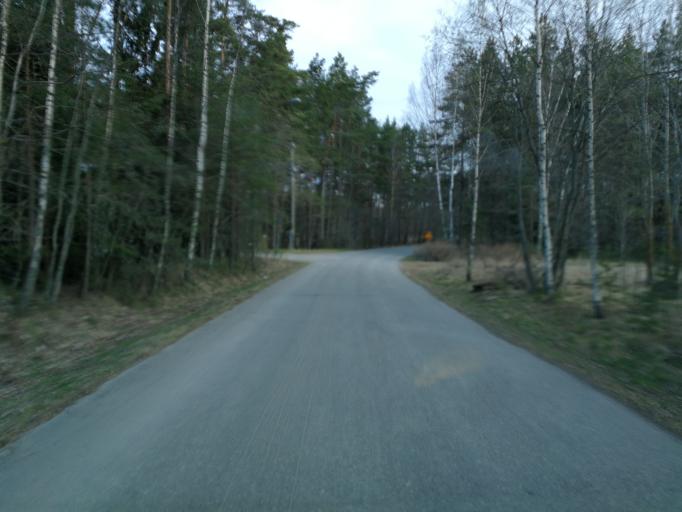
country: FI
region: Varsinais-Suomi
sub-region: Turku
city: Kaarina
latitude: 60.4180
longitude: 22.3185
